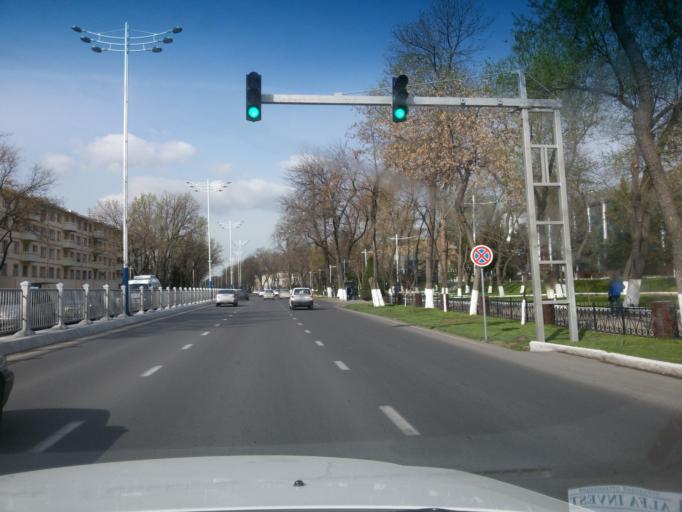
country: UZ
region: Toshkent
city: Salor
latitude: 41.3256
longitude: 69.3240
